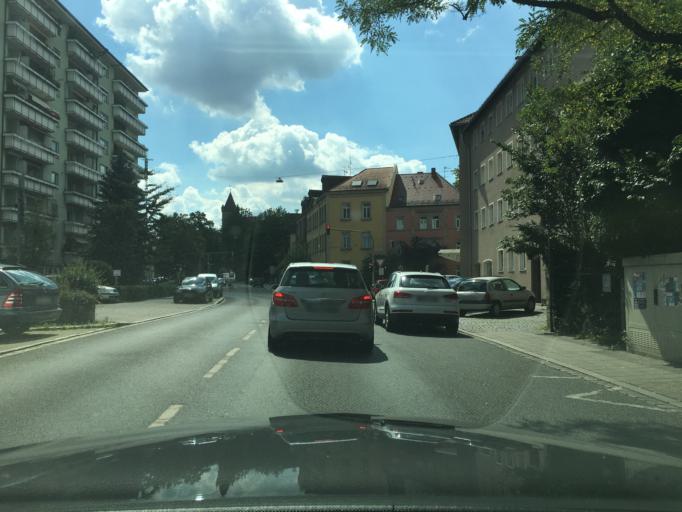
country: DE
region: Bavaria
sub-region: Regierungsbezirk Mittelfranken
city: Nuernberg
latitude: 49.4615
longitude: 11.0755
